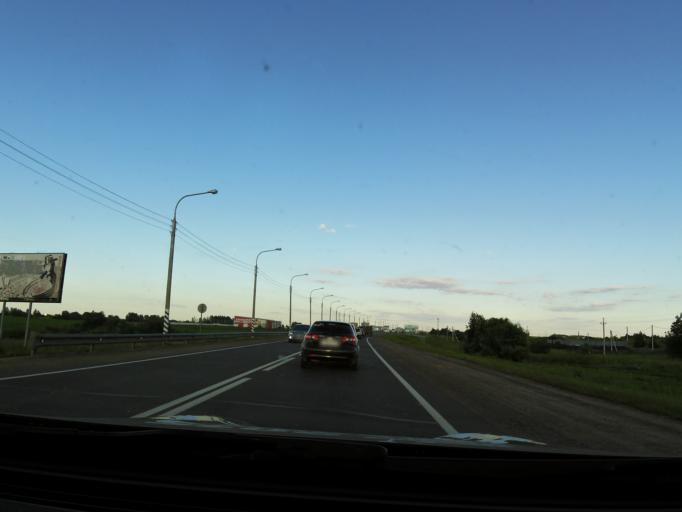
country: RU
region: Vologda
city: Vologda
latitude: 59.1751
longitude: 39.8962
